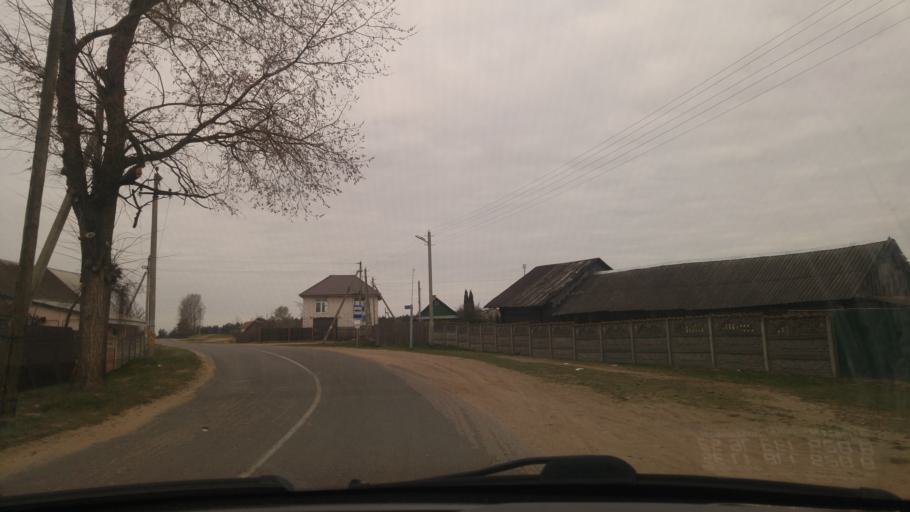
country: BY
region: Minsk
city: Smilavichy
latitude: 53.7140
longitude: 28.1392
